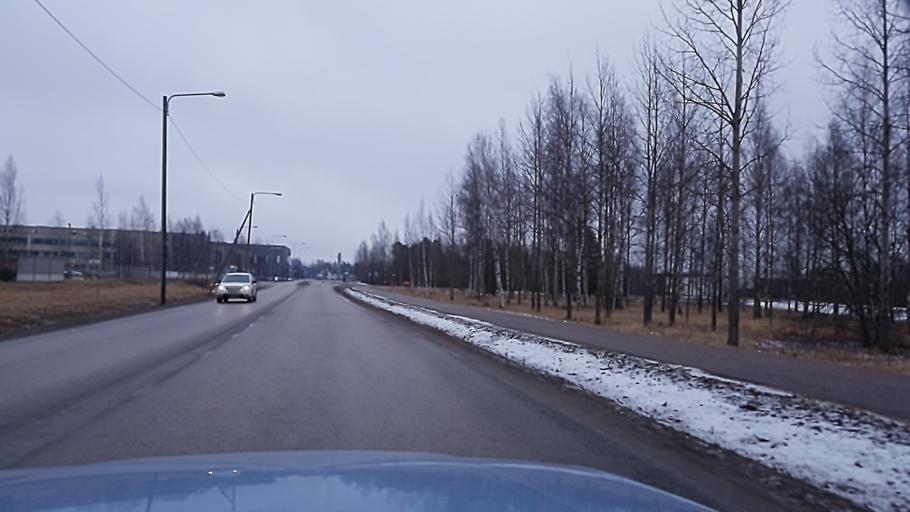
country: FI
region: Uusimaa
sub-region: Helsinki
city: Vantaa
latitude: 60.2968
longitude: 24.9736
